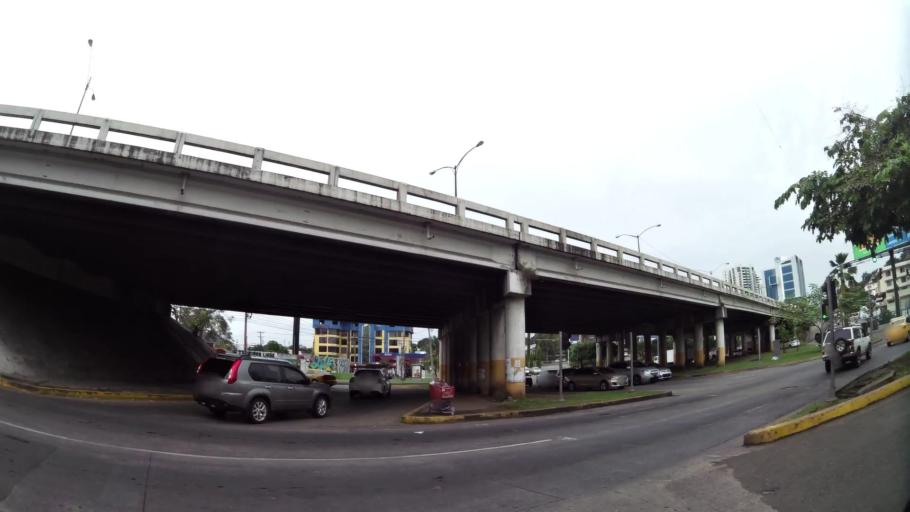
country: PA
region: Panama
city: Panama
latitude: 8.9881
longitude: -79.5329
